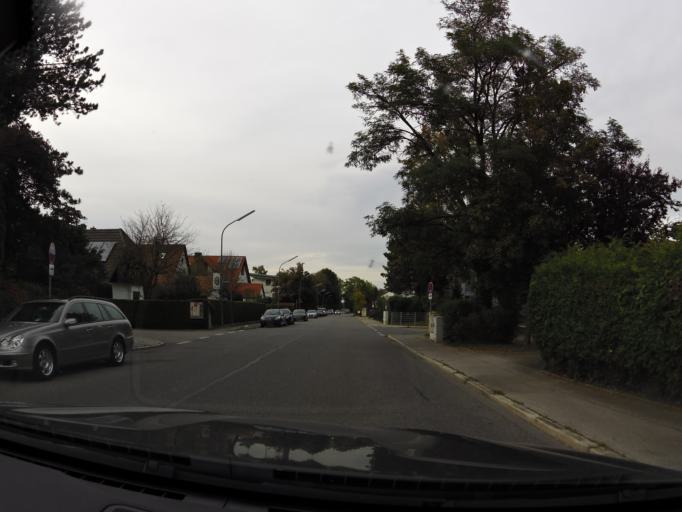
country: DE
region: Bavaria
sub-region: Upper Bavaria
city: Grobenzell
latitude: 48.1832
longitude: 11.3710
